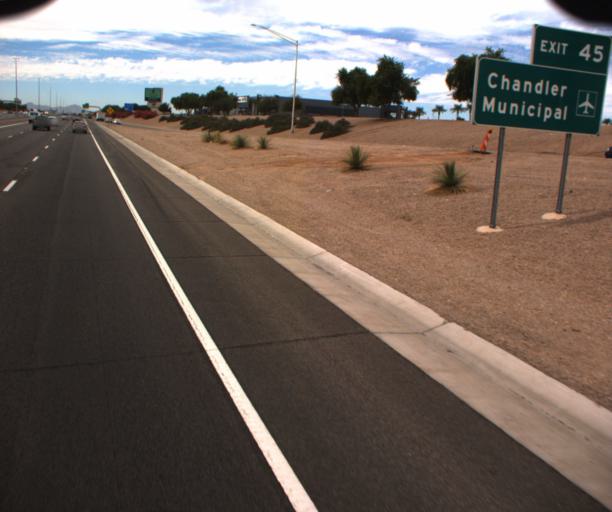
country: US
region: Arizona
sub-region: Maricopa County
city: Chandler
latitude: 33.2831
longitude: -111.7915
